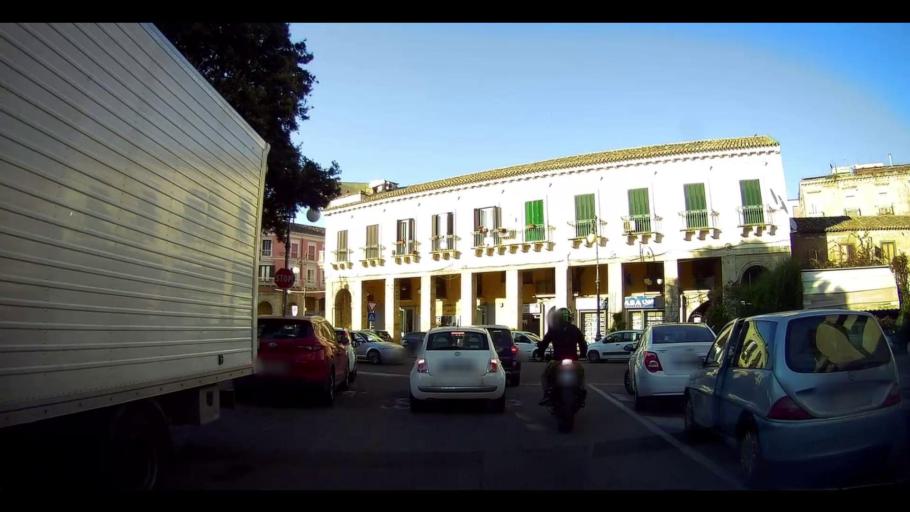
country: IT
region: Calabria
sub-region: Provincia di Crotone
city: Crotone
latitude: 39.0801
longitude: 17.1275
